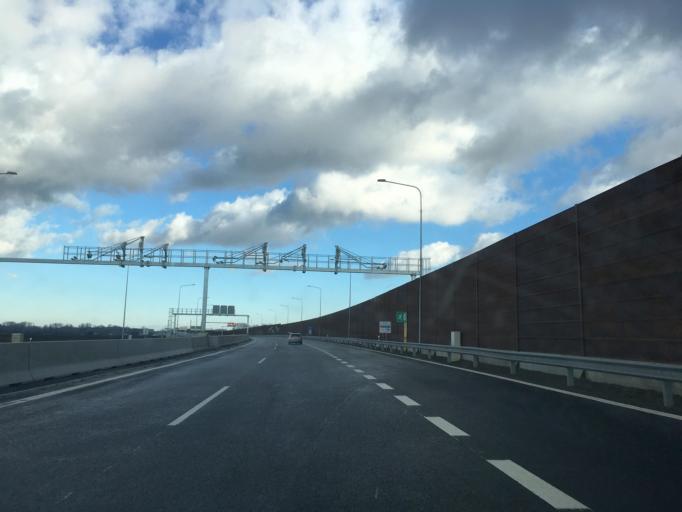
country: AT
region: Burgenland
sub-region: Politischer Bezirk Neusiedl am See
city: Kittsee
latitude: 48.0717
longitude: 17.1091
